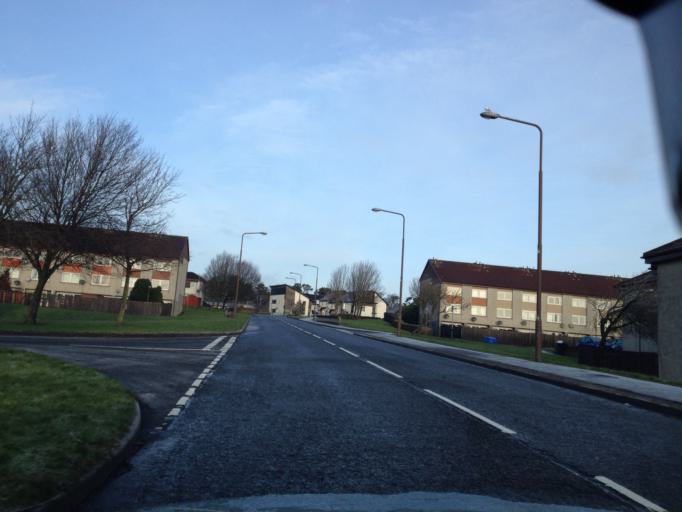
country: GB
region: Scotland
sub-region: West Lothian
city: Mid Calder
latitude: 55.9011
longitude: -3.4917
